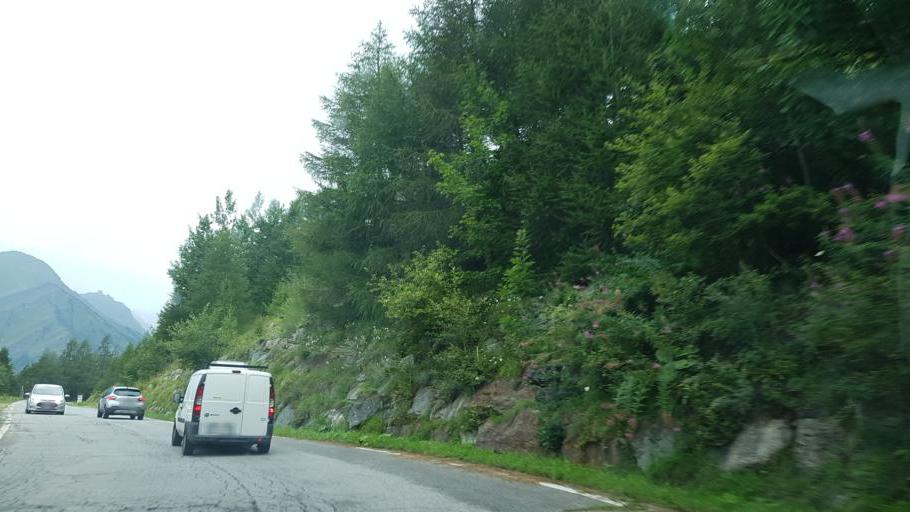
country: IT
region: Piedmont
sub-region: Provincia di Cuneo
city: Casteldelfino
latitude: 44.6091
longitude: 7.0598
